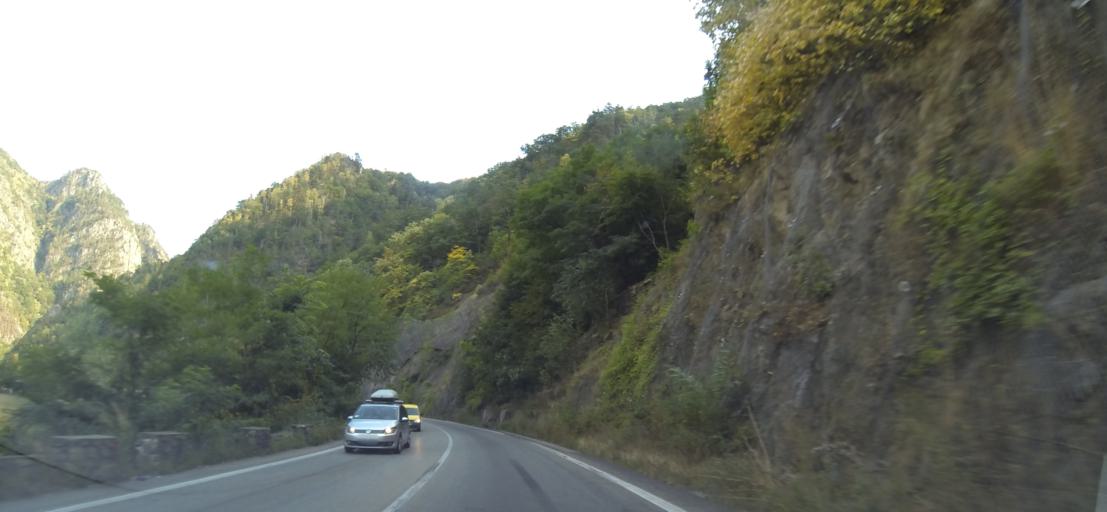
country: RO
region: Valcea
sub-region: Comuna Brezoi
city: Brezoi
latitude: 45.2998
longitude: 24.2839
